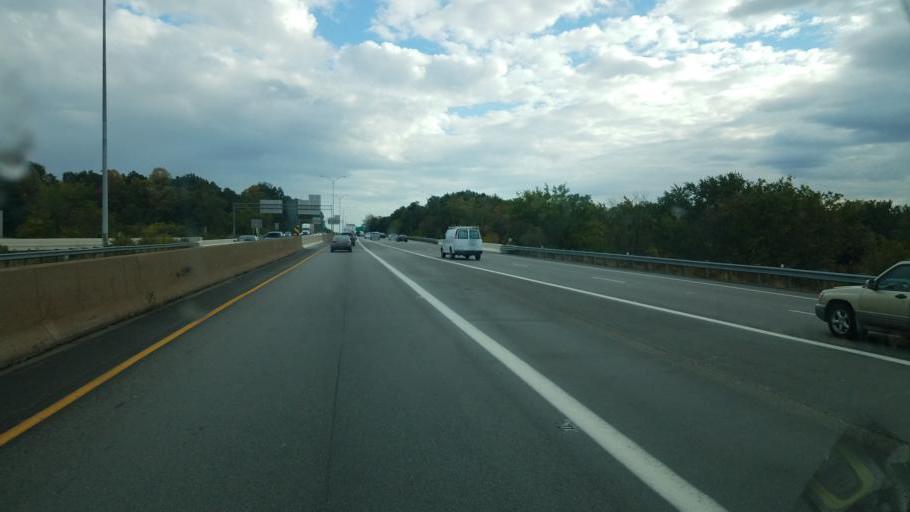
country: US
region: Ohio
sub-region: Summit County
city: Akron
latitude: 41.0597
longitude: -81.5681
